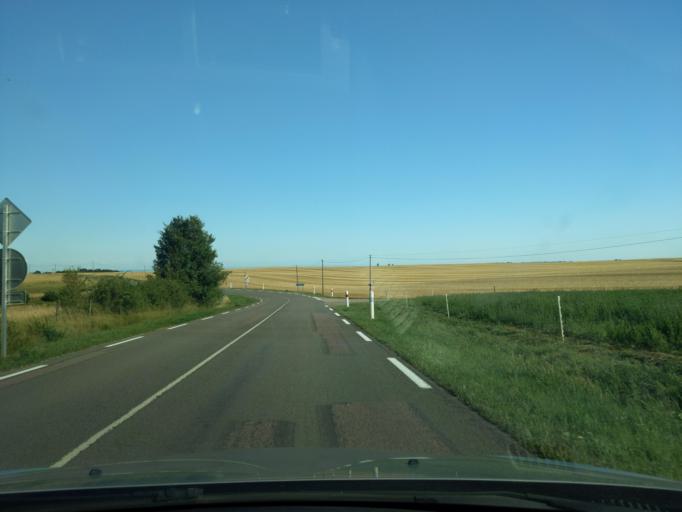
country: FR
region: Bourgogne
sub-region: Departement de la Cote-d'Or
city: Is-sur-Tille
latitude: 47.4981
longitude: 5.0865
